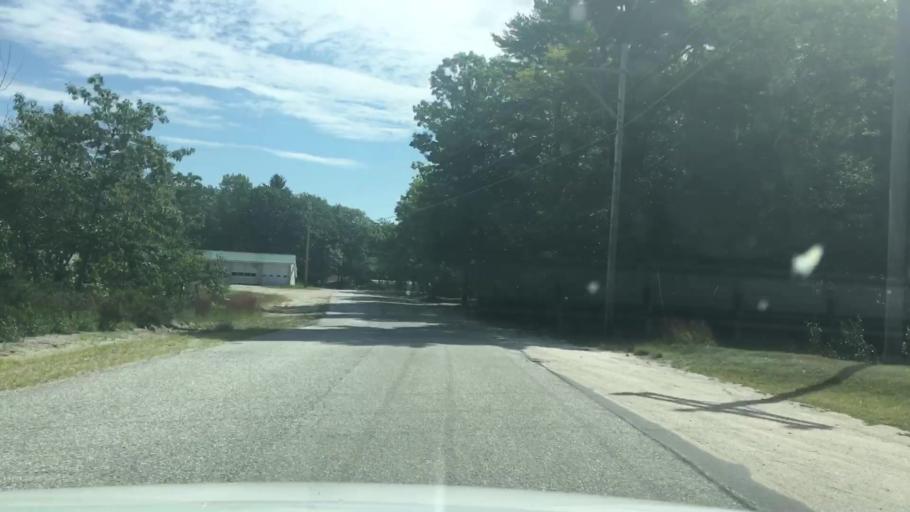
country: US
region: Maine
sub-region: Androscoggin County
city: Turner
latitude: 44.1921
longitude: -70.2457
